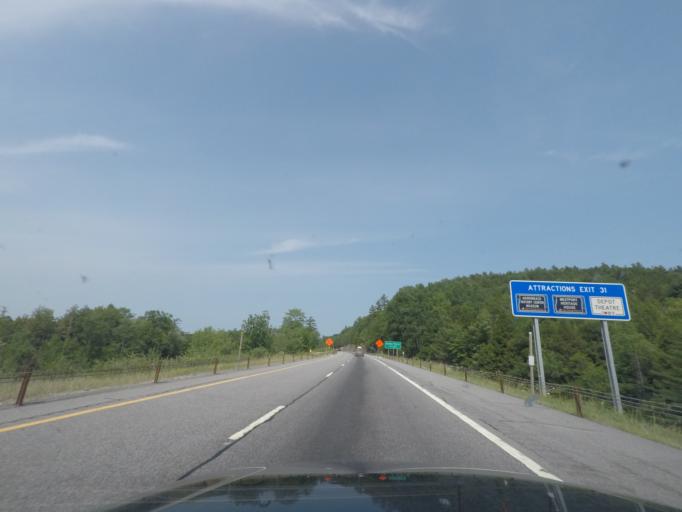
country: US
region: New York
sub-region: Essex County
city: Elizabethtown
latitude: 44.1995
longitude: -73.5160
